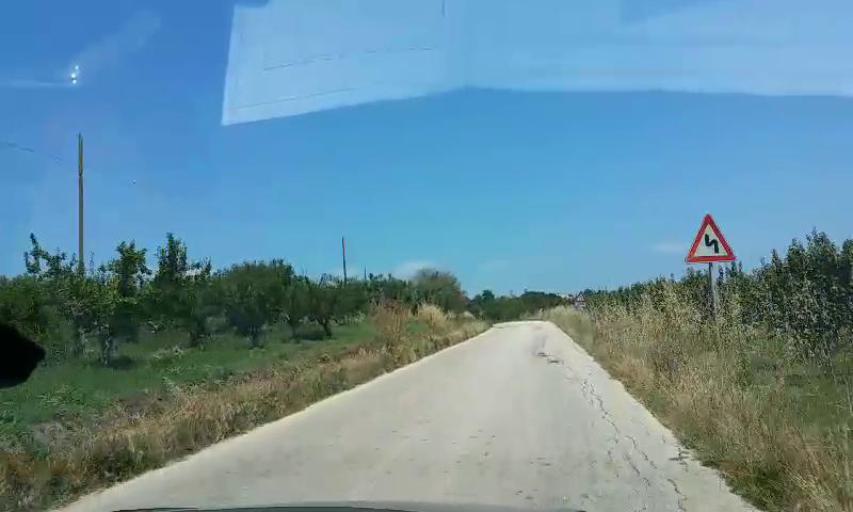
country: IT
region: Molise
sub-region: Provincia di Campobasso
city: San Giacomo degli Schiavoni
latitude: 41.9705
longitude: 14.9023
